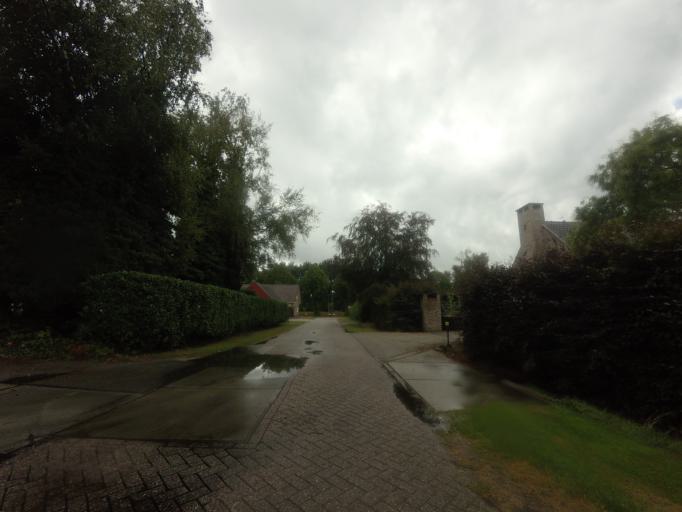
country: NL
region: Overijssel
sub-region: Gemeente Dalfsen
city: Dalfsen
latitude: 52.5995
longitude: 6.3735
